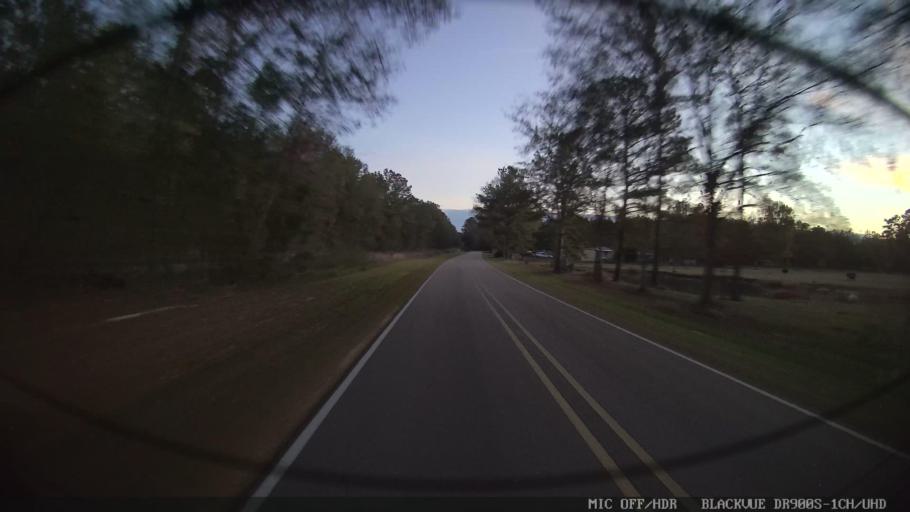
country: US
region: Mississippi
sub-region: Perry County
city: New Augusta
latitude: 31.0904
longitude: -89.1882
